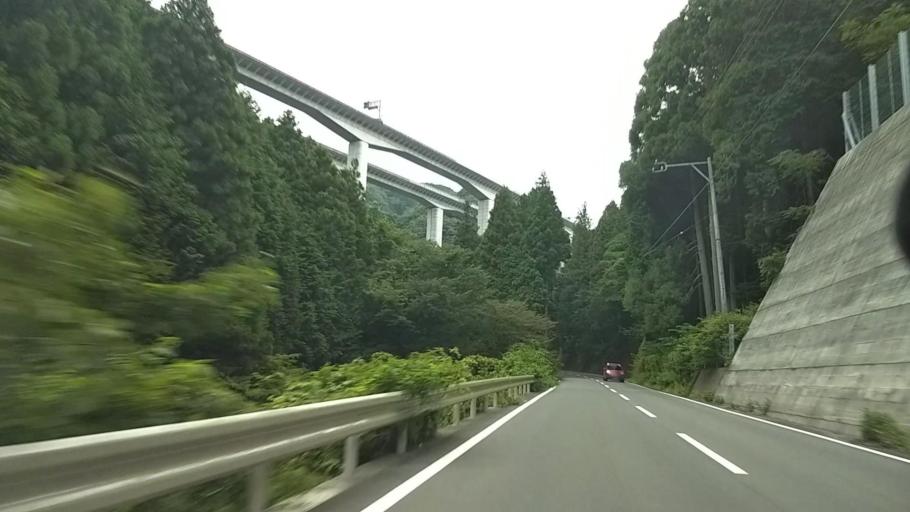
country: JP
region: Shizuoka
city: Fujinomiya
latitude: 35.1576
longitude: 138.5407
